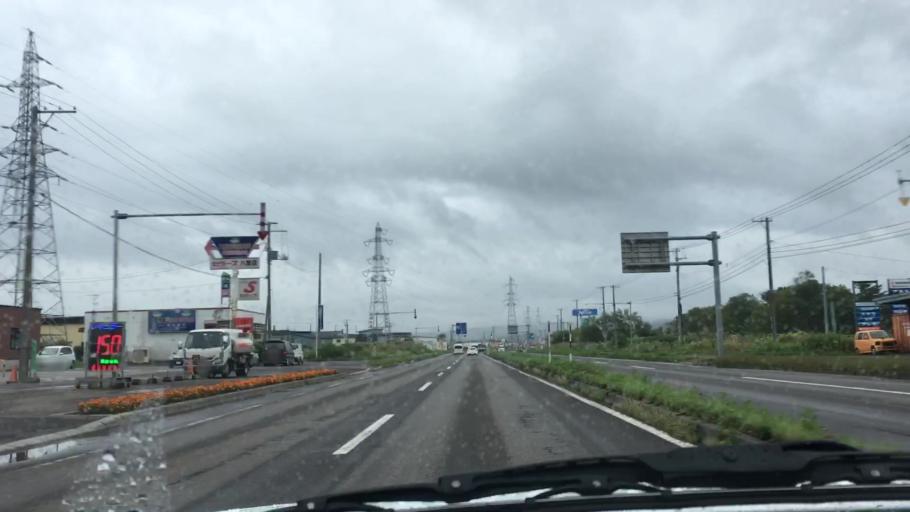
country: JP
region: Hokkaido
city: Nanae
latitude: 42.2562
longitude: 140.2807
